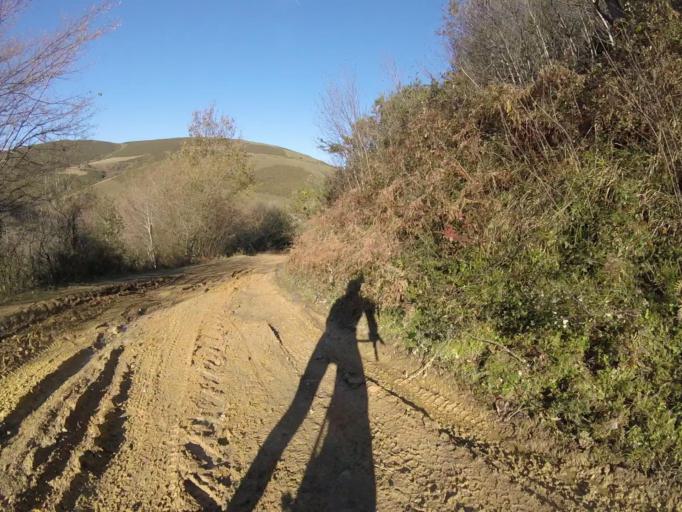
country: ES
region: Navarre
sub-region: Provincia de Navarra
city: Bera
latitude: 43.3176
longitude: -1.7118
